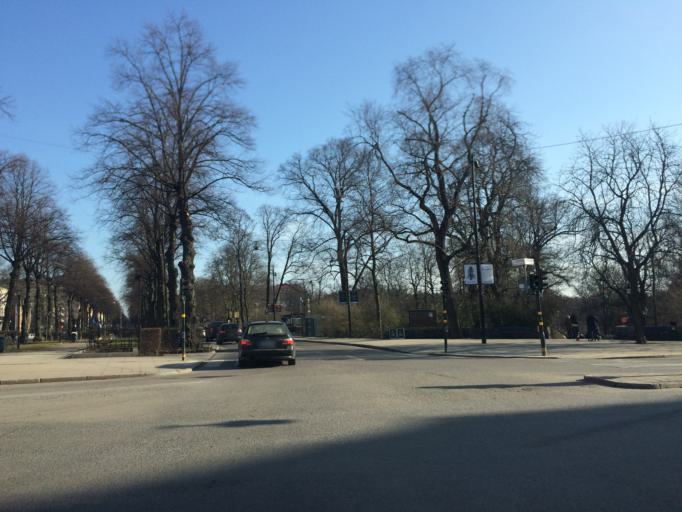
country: SE
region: Stockholm
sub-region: Stockholms Kommun
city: Stockholm
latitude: 59.3417
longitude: 18.0705
